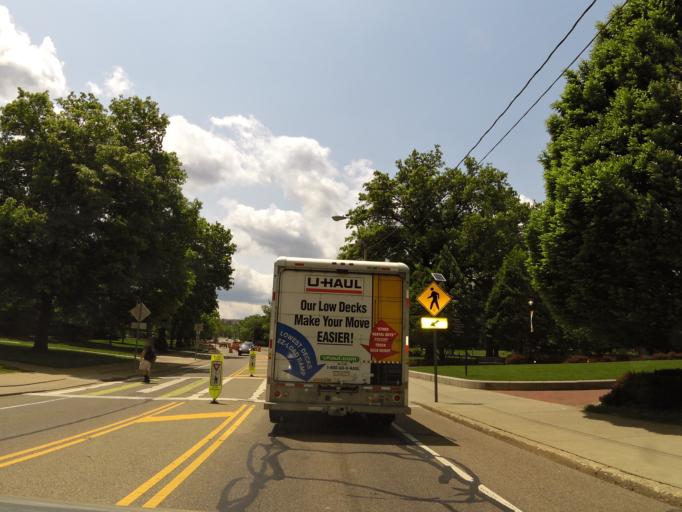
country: US
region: Ohio
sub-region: Athens County
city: Athens
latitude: 39.3248
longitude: -82.1040
